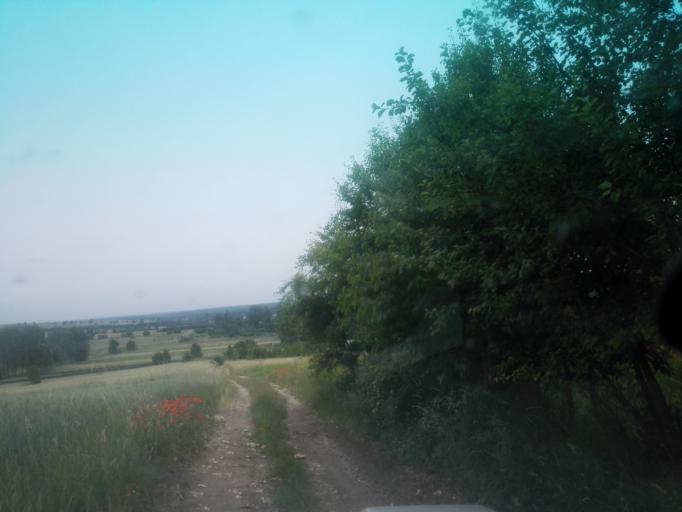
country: PL
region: Silesian Voivodeship
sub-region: Powiat czestochowski
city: Mstow
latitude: 50.7992
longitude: 19.3612
